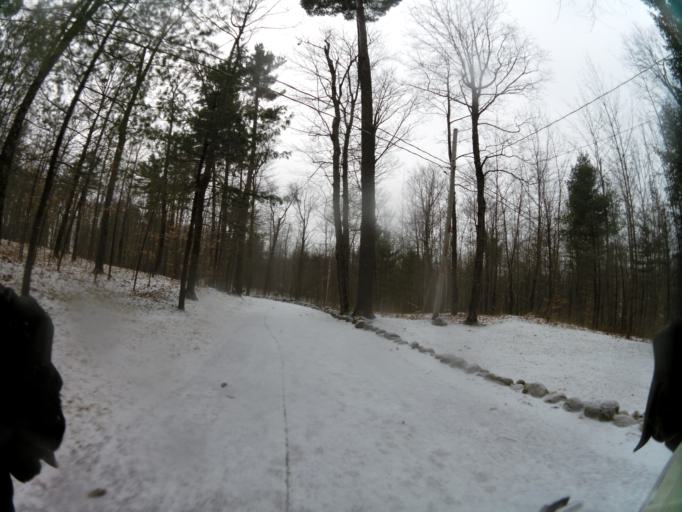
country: CA
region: Quebec
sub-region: Outaouais
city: Gatineau
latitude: 45.4860
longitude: -75.8476
